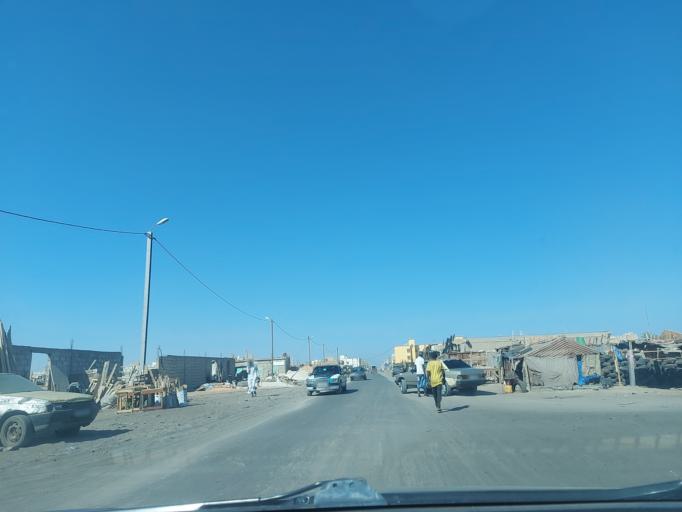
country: MR
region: Nouakchott
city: Nouakchott
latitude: 18.0678
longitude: -15.9952
